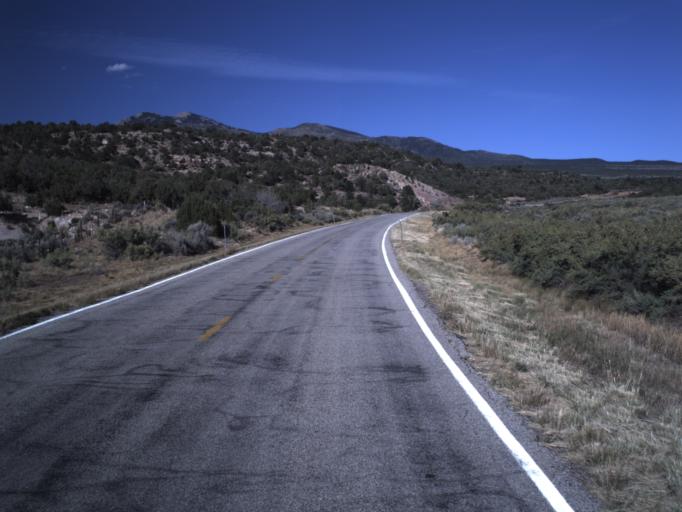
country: US
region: Utah
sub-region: Grand County
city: Moab
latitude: 38.3157
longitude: -109.3508
